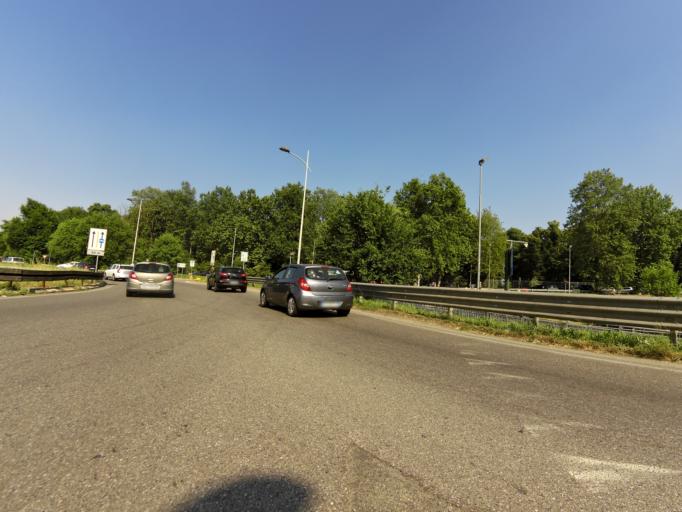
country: IT
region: Lombardy
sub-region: Citta metropolitana di Milano
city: Novegro-Tregarezzo-San Felice
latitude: 45.4733
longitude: 9.2860
